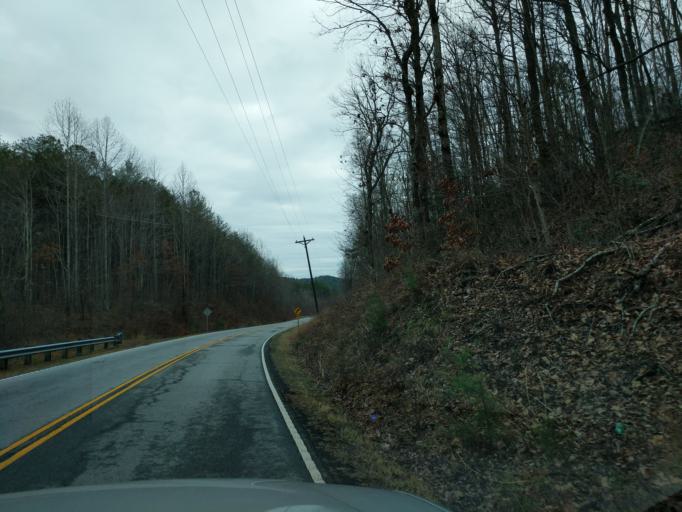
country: US
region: South Carolina
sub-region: Oconee County
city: Westminster
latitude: 34.7370
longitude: -83.2349
